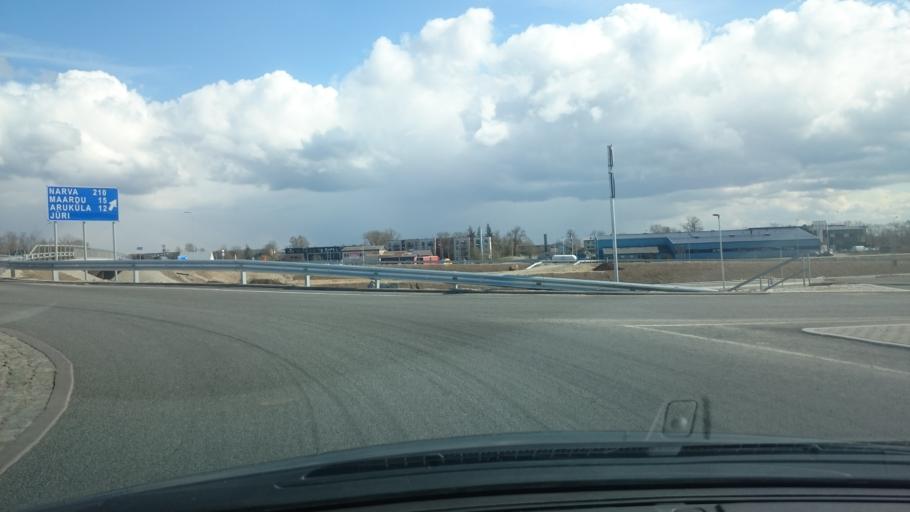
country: EE
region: Harju
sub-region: Rae vald
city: Jueri
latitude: 59.3586
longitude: 24.8896
